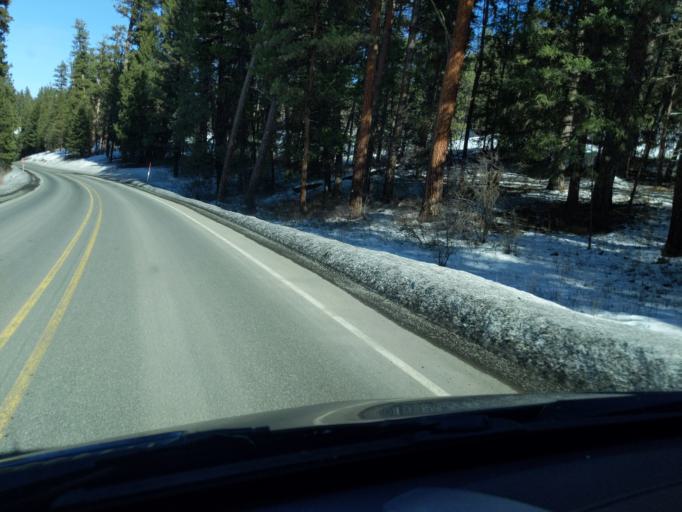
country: US
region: Oregon
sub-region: Grant County
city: John Day
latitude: 44.9418
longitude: -118.9991
